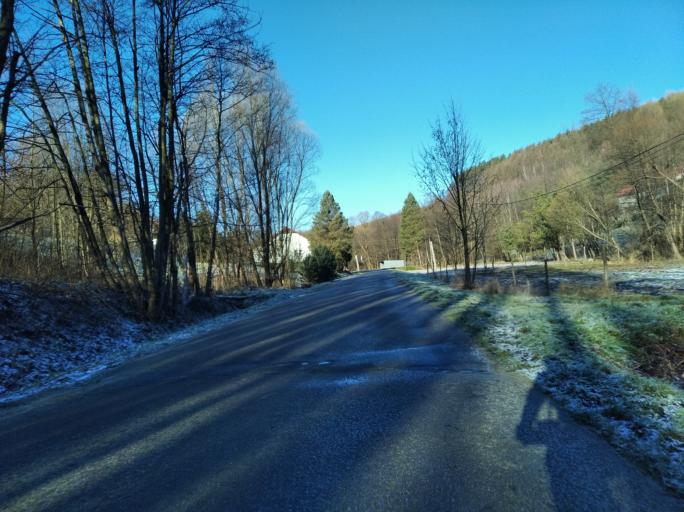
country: PL
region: Subcarpathian Voivodeship
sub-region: Powiat strzyzowski
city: Czudec
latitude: 49.9458
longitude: 21.7856
